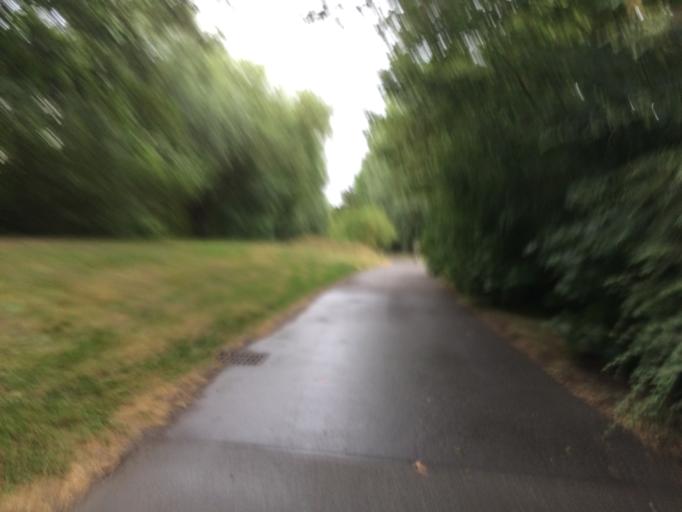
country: FR
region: Picardie
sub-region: Departement de l'Oise
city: Venette
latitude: 49.4058
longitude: 2.7976
